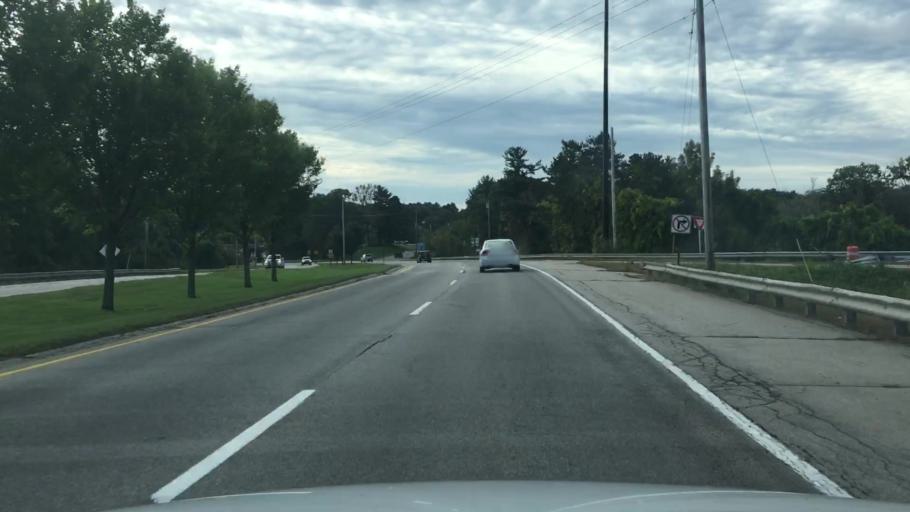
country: US
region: Maine
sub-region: York County
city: Kittery
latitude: 43.1037
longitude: -70.7474
